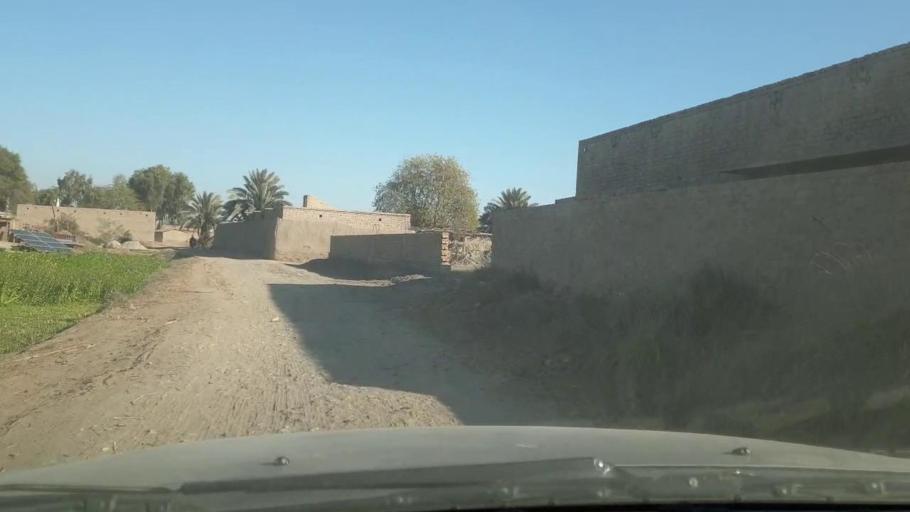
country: PK
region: Sindh
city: Adilpur
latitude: 27.9605
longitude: 69.2068
